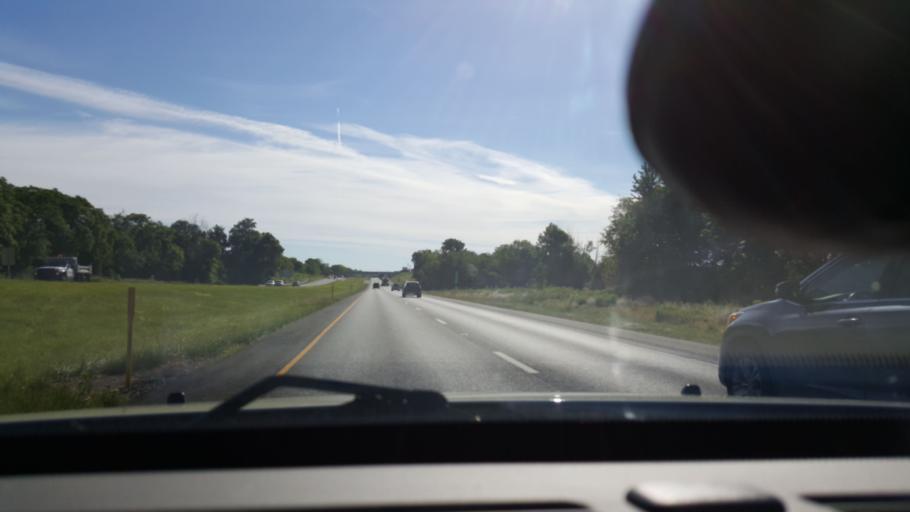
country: US
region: Pennsylvania
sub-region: York County
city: Yorklyn
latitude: 39.9972
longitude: -76.6448
